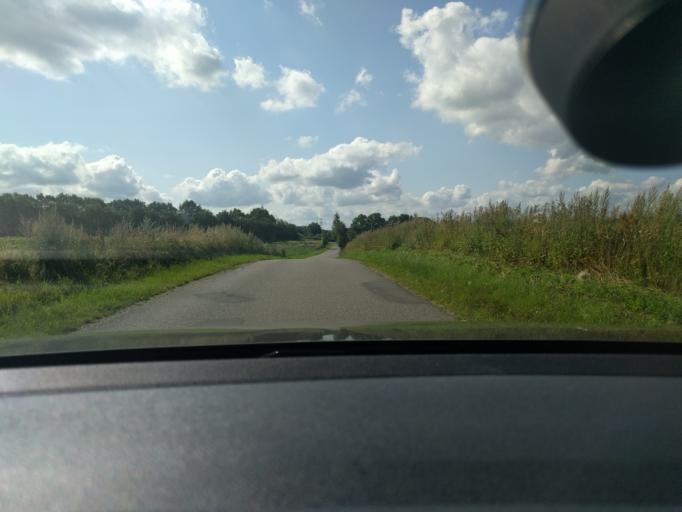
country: DK
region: Central Jutland
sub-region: Viborg Kommune
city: Viborg
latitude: 56.5048
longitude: 9.5060
